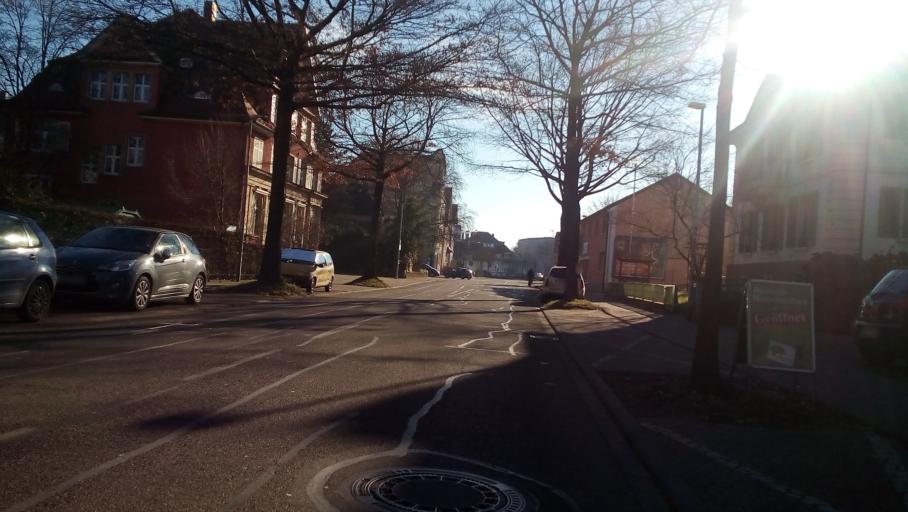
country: DE
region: Baden-Wuerttemberg
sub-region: Freiburg Region
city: Achern
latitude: 48.6313
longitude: 8.0674
